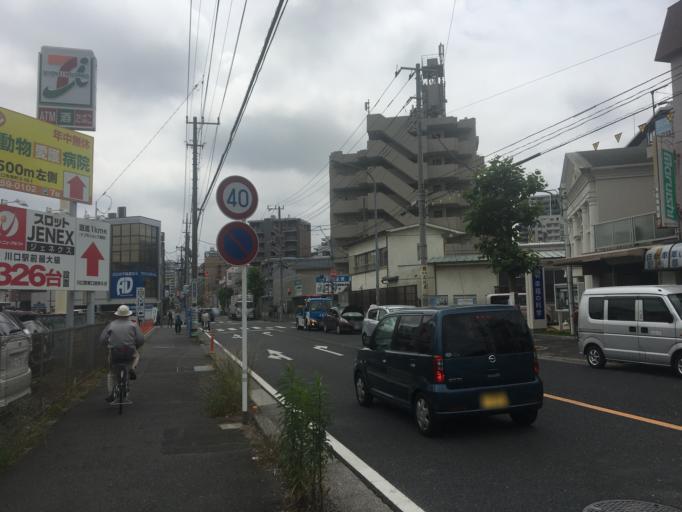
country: JP
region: Saitama
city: Kawaguchi
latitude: 35.8118
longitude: 139.7137
